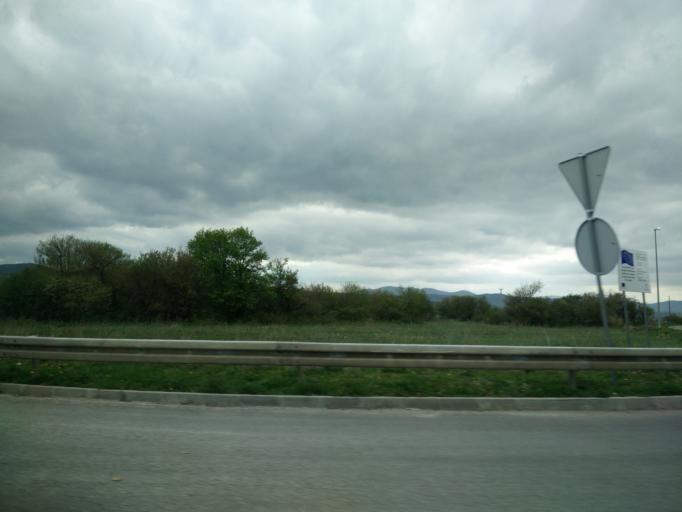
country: HR
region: Zadarska
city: Gracac
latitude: 44.5429
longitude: 15.7558
